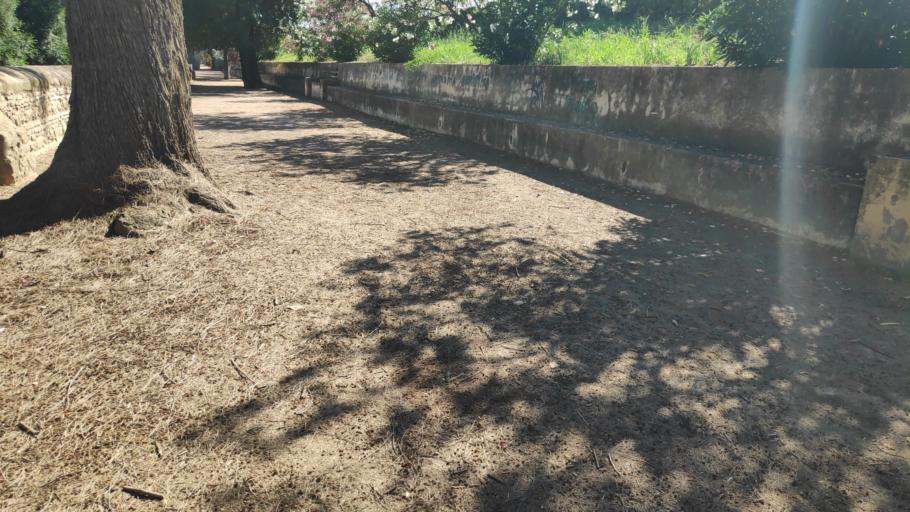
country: ES
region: Andalusia
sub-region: Province of Cordoba
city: Cordoba
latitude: 37.8748
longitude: -4.7822
